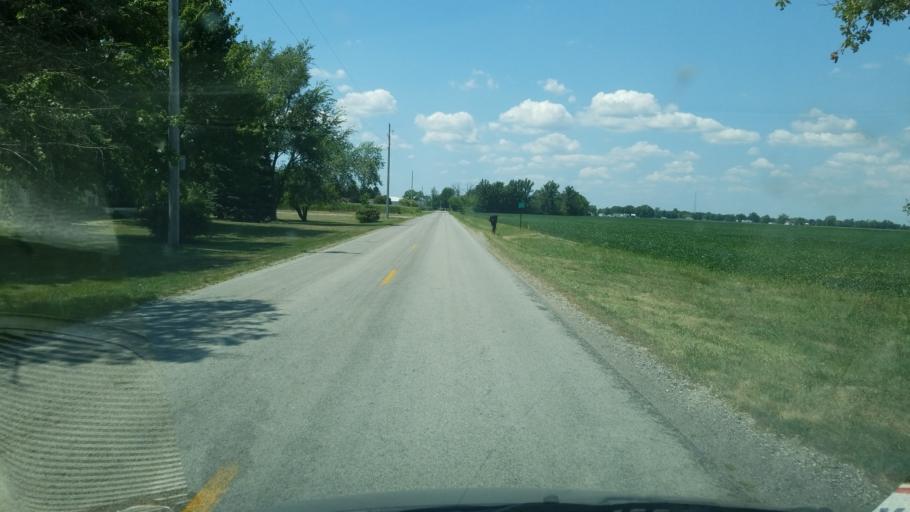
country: US
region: Ohio
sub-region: Madison County
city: Plain City
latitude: 40.0427
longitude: -83.3750
